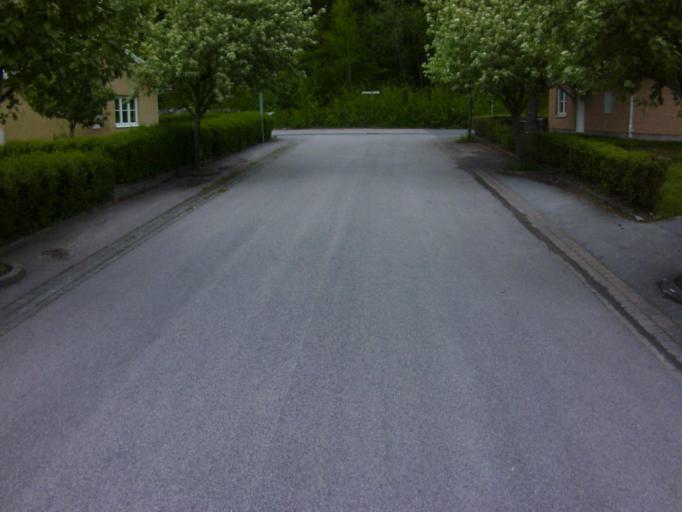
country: SE
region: Blekinge
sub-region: Solvesborgs Kommun
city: Soelvesborg
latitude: 56.0492
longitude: 14.5601
